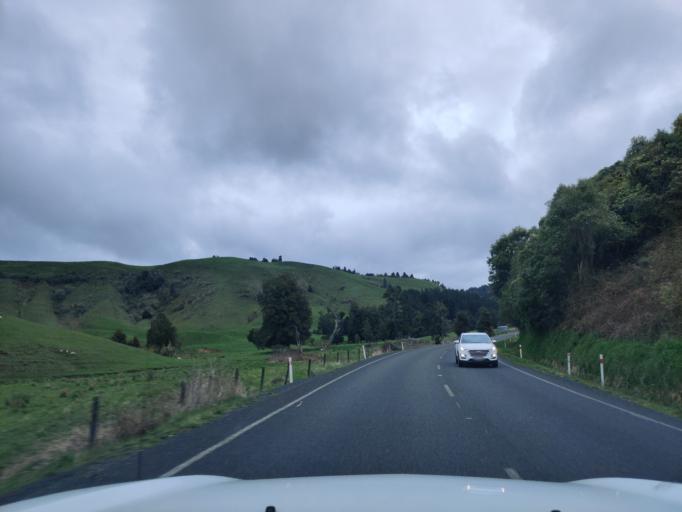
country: NZ
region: Waikato
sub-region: Otorohanga District
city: Otorohanga
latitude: -38.5511
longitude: 175.1915
